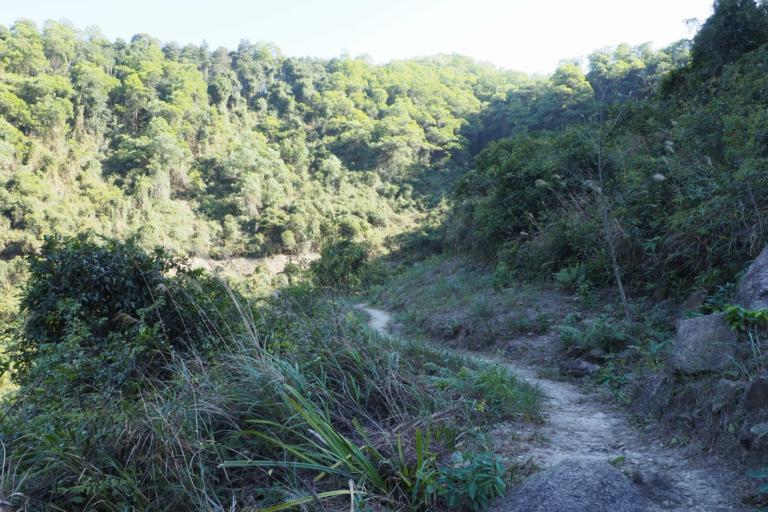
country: CN
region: Guangdong
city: Dongqu
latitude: 22.4755
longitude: 113.4177
